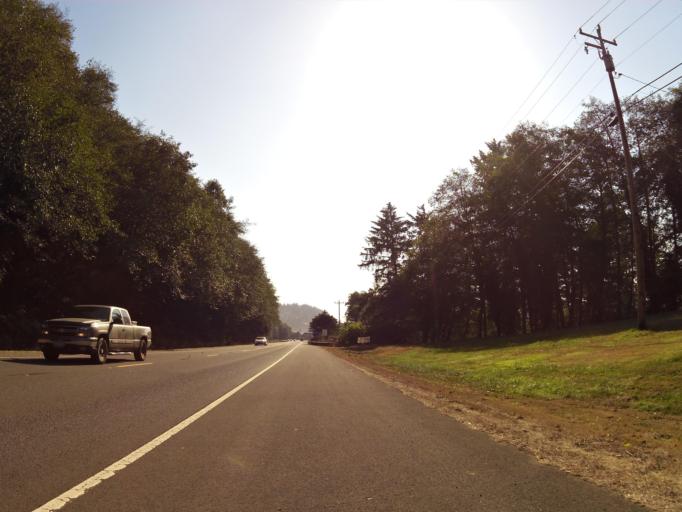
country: US
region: Oregon
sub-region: Tillamook County
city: Pacific City
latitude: 45.1071
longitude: -123.9772
